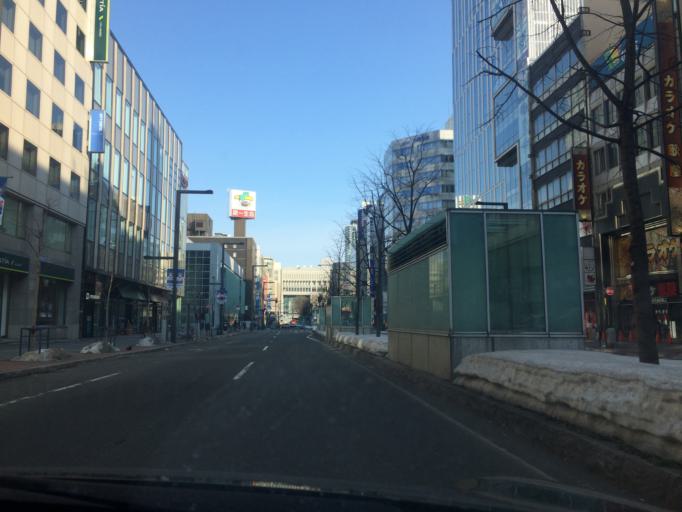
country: JP
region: Hokkaido
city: Sapporo
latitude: 43.0633
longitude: 141.3513
